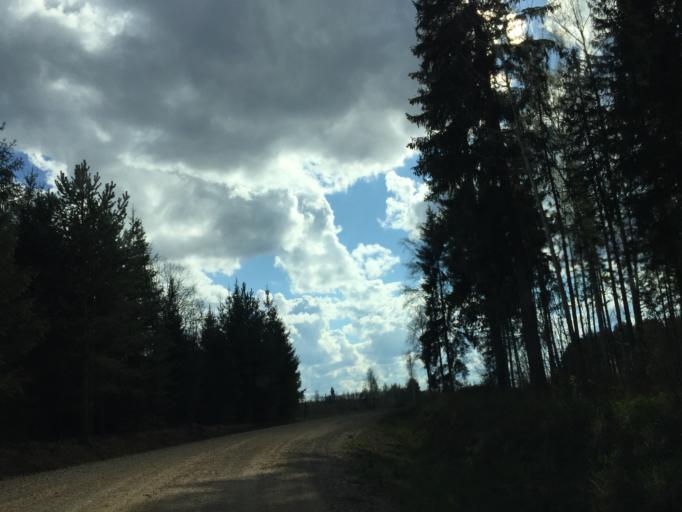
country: LV
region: Beverina
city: Murmuiza
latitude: 57.4748
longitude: 25.5078
